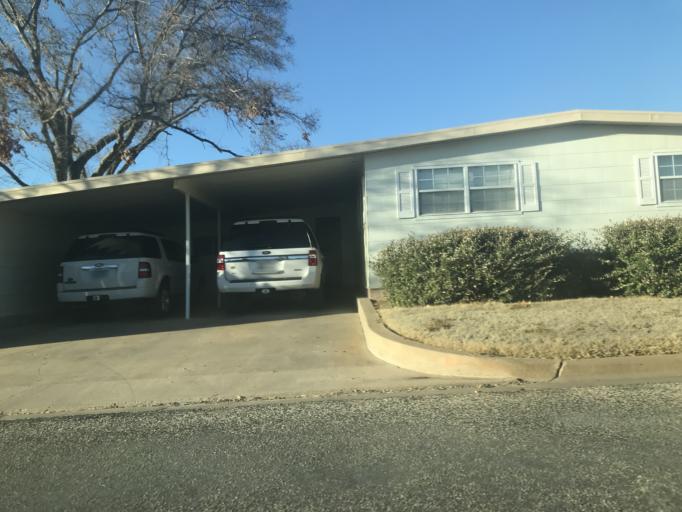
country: US
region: Texas
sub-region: Tom Green County
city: San Angelo
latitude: 31.4384
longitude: -100.4751
